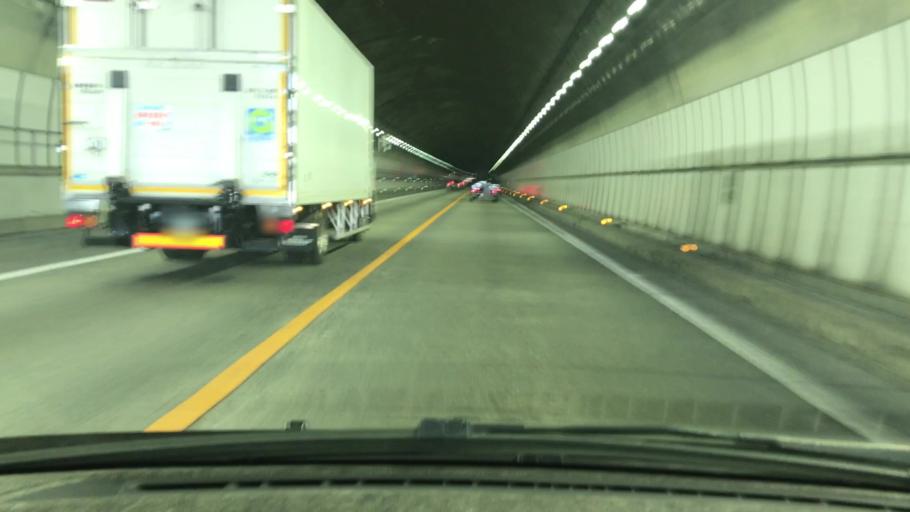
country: JP
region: Osaka
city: Takatsuki
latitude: 34.8693
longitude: 135.6501
